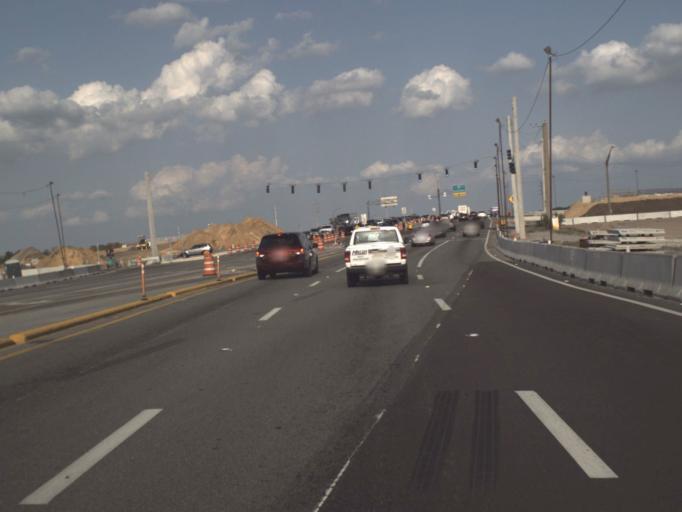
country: US
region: Florida
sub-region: Orange County
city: Eatonville
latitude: 28.6307
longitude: -81.3910
